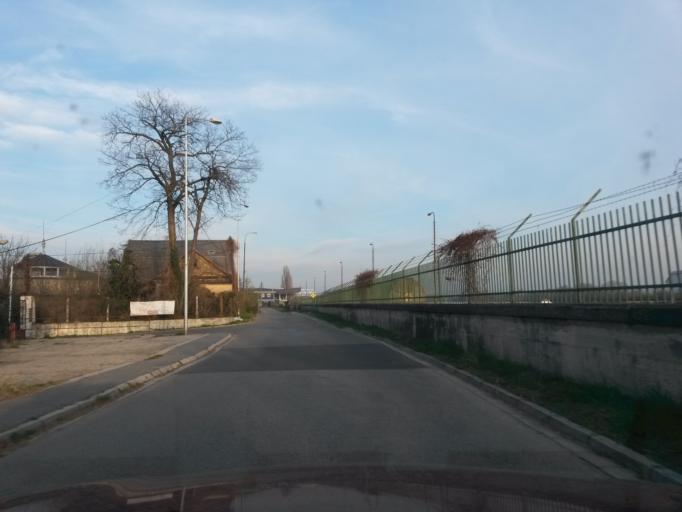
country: SK
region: Nitriansky
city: Komarno
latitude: 47.7510
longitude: 18.1396
